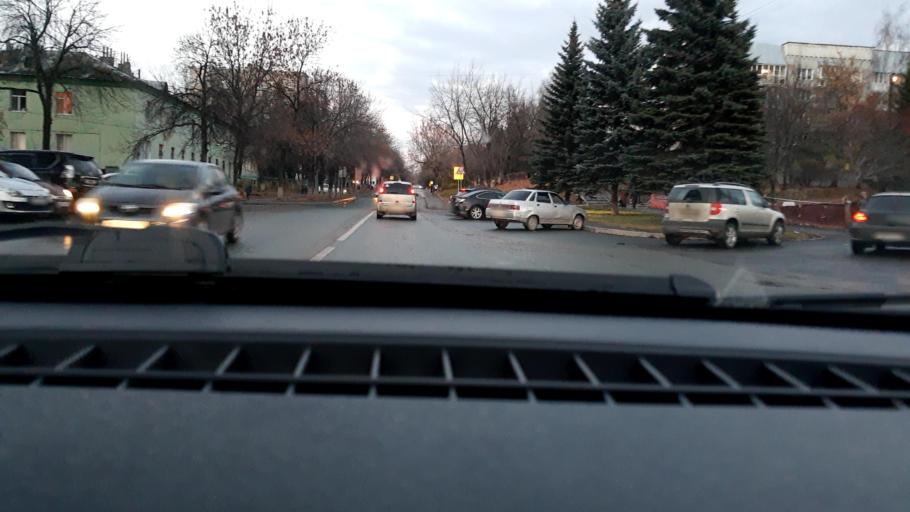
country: RU
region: Bashkortostan
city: Ufa
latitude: 54.8141
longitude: 56.0657
